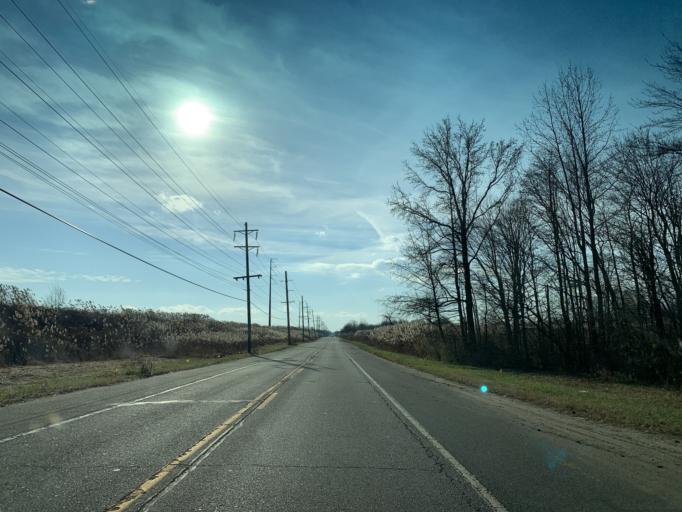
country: US
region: Pennsylvania
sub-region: Delaware County
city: Marcus Hook
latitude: 39.7835
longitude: -75.4084
